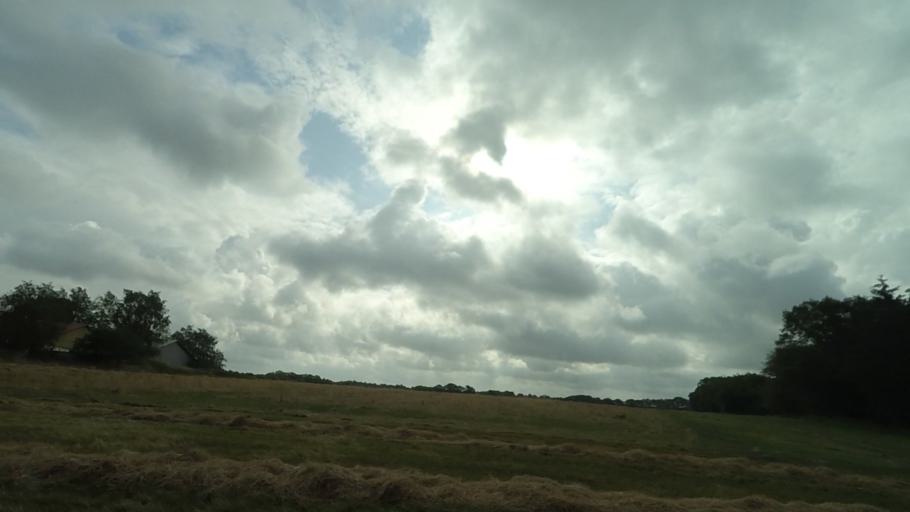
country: DK
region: Central Jutland
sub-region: Syddjurs Kommune
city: Ryomgard
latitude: 56.3972
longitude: 10.4892
